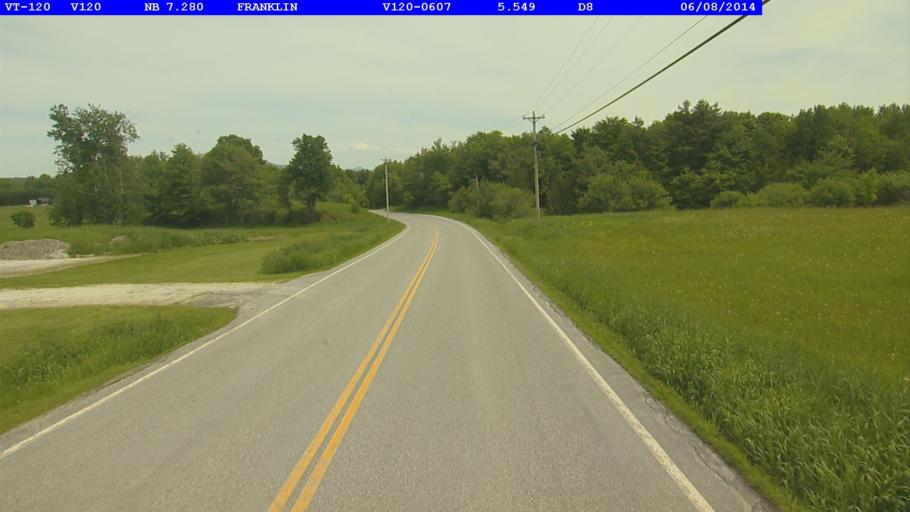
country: US
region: Vermont
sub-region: Franklin County
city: Enosburg Falls
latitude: 44.9866
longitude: -72.8823
